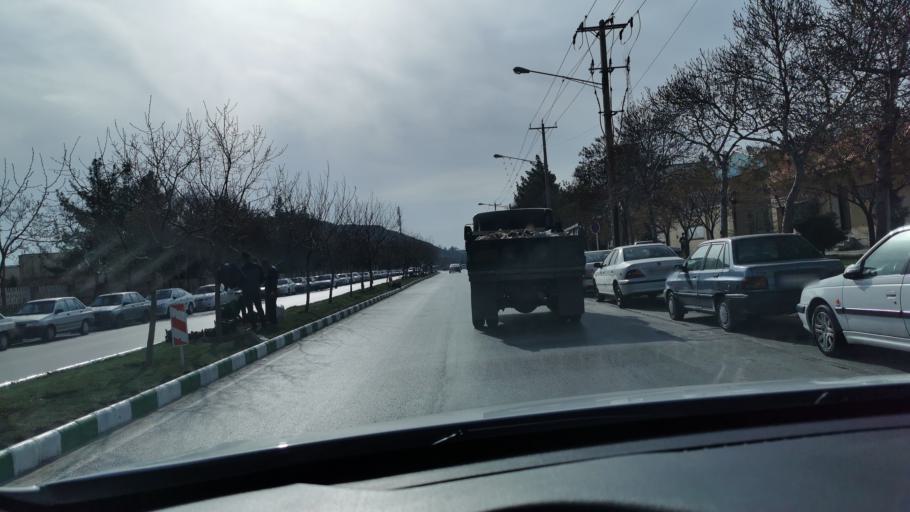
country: IR
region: Razavi Khorasan
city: Mashhad
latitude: 36.2823
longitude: 59.5517
